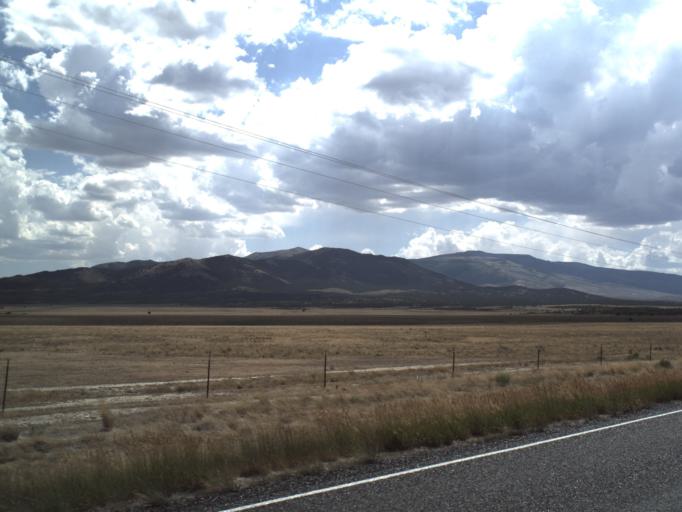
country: US
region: Idaho
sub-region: Minidoka County
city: Rupert
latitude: 41.9705
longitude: -113.1266
